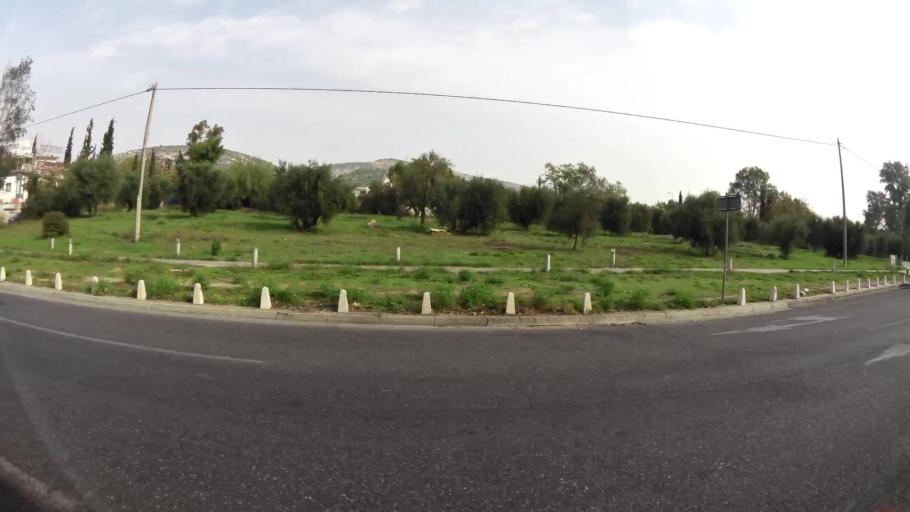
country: GR
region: Attica
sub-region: Nomarchia Athinas
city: Chaidari
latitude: 38.0124
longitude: 23.6394
